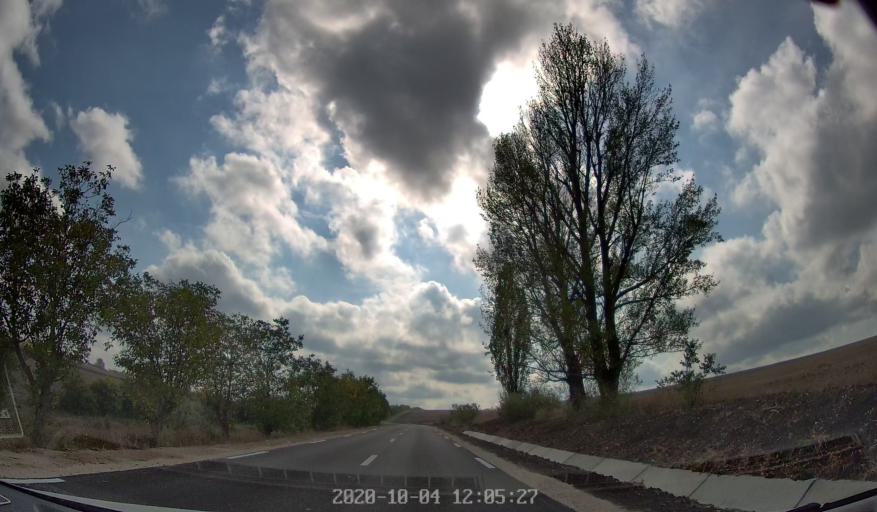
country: MD
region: Rezina
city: Saharna
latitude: 47.5939
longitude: 28.9504
